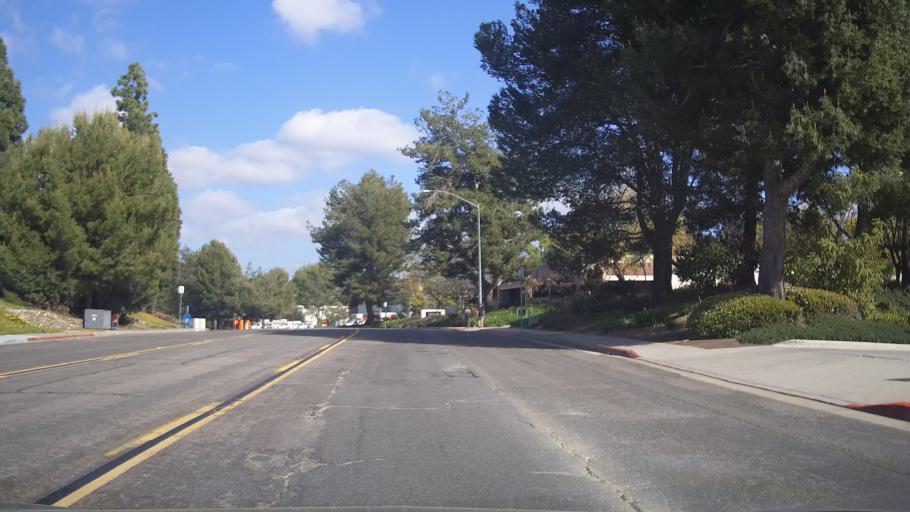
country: US
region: California
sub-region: San Diego County
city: Poway
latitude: 32.9873
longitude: -117.0702
